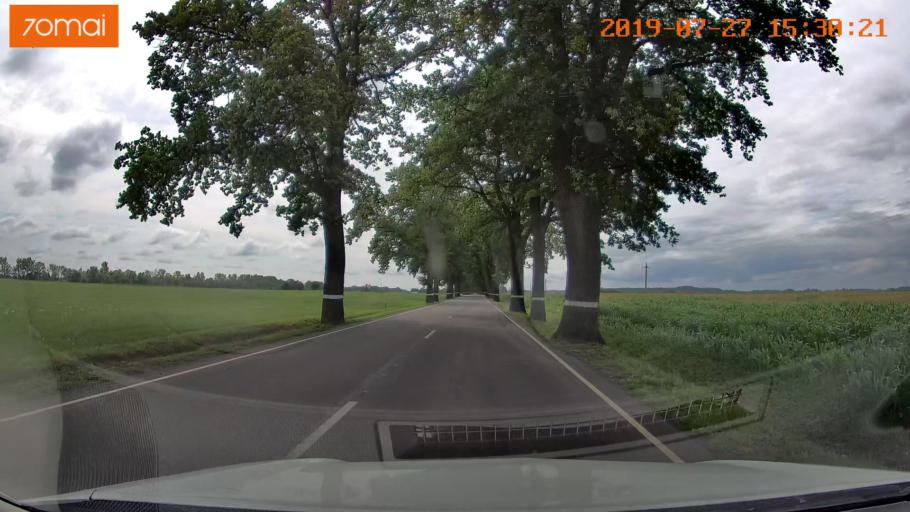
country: RU
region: Kaliningrad
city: Nesterov
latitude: 54.6281
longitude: 22.5134
